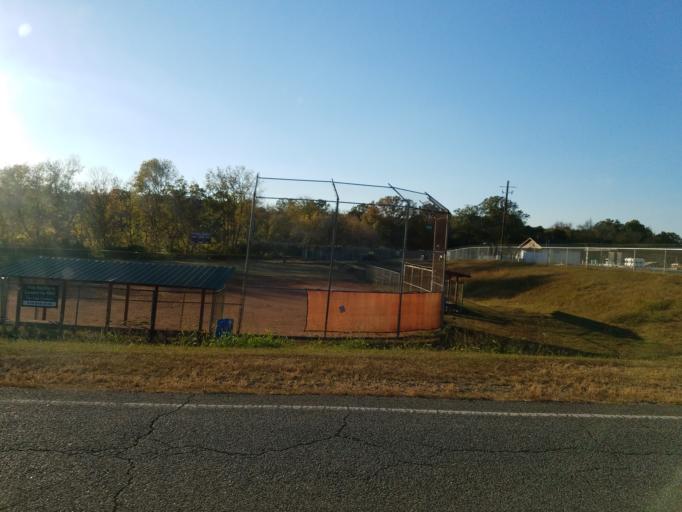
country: US
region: Georgia
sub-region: Bartow County
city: Adairsville
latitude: 34.3731
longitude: -84.9405
